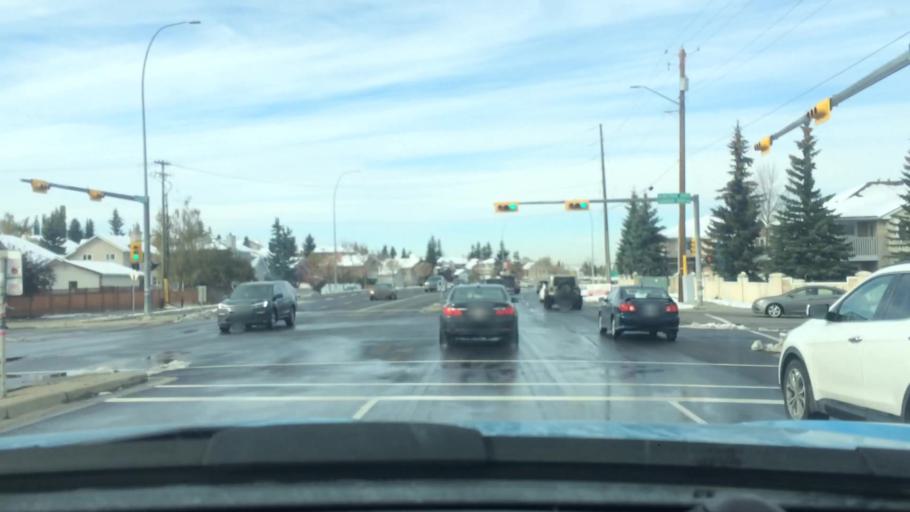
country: CA
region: Alberta
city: Calgary
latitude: 51.1400
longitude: -114.1086
